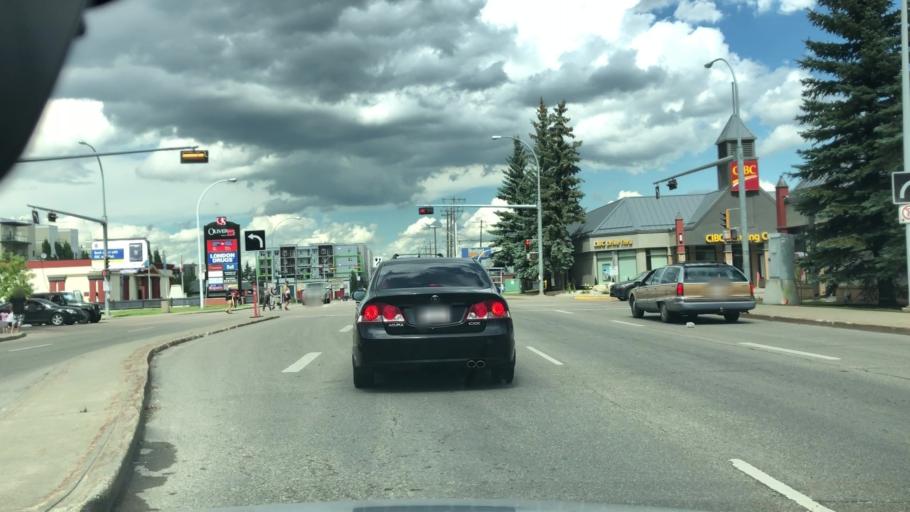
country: CA
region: Alberta
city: Edmonton
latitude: 53.5469
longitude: -113.5213
